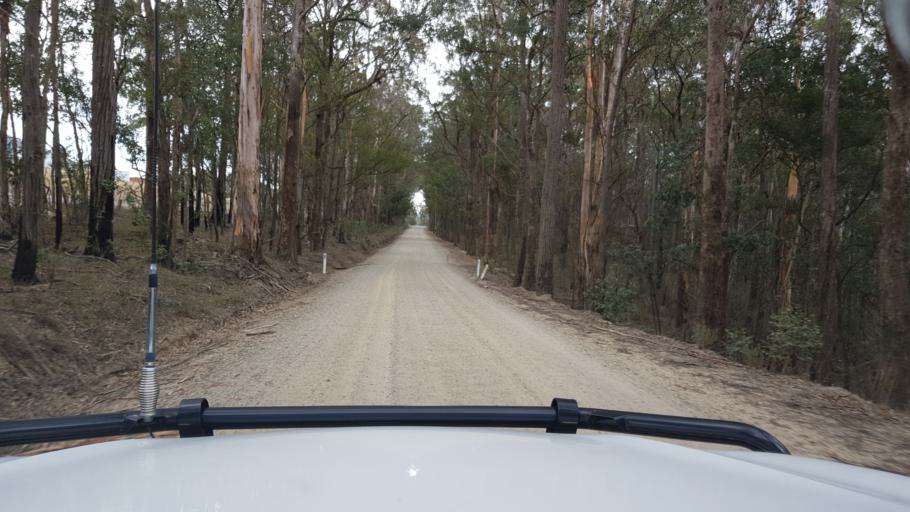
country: AU
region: Victoria
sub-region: East Gippsland
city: Bairnsdale
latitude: -37.6876
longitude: 147.5611
